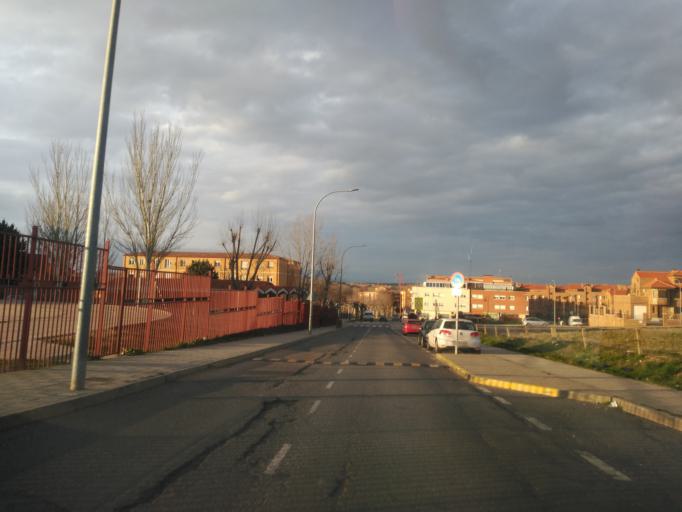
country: ES
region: Castille and Leon
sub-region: Provincia de Salamanca
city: Santa Marta de Tormes
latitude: 40.9461
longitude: -5.6321
